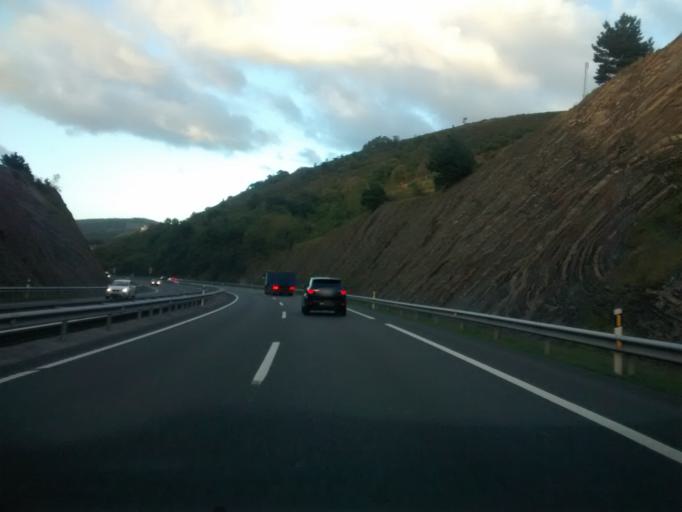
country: ES
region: Basque Country
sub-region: Provincia de Guipuzcoa
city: Zumaia
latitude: 43.2724
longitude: -2.2575
